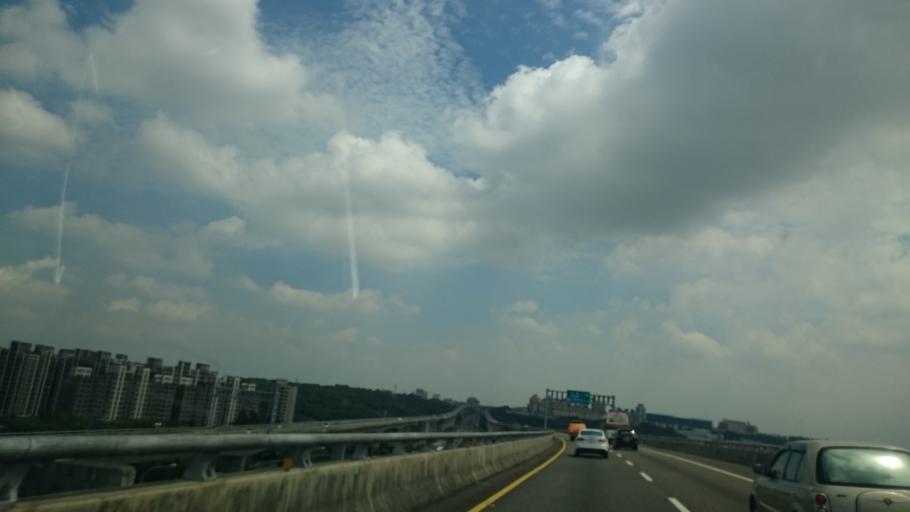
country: TW
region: Taiwan
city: Daxi
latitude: 24.9068
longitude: 121.1638
